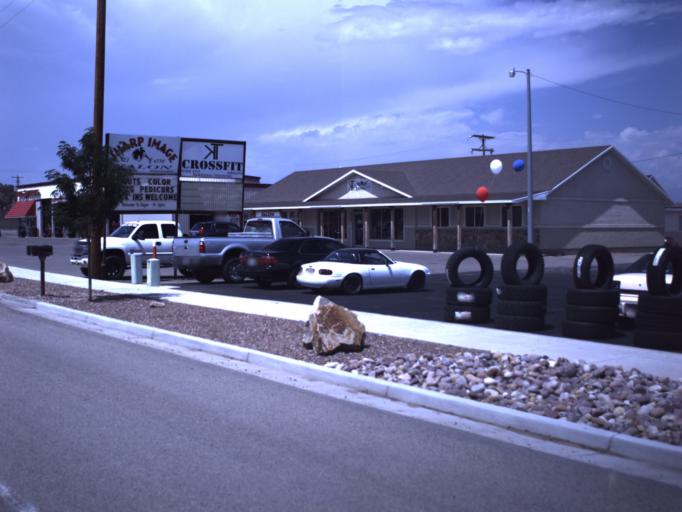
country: US
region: Utah
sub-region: Duchesne County
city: Roosevelt
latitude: 40.3023
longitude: -109.9713
